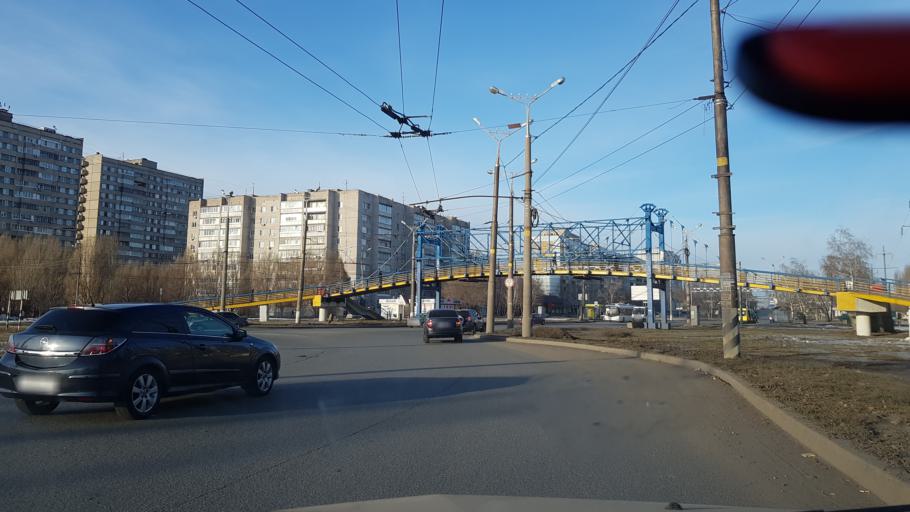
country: RU
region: Samara
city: Tol'yatti
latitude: 53.5294
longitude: 49.3971
